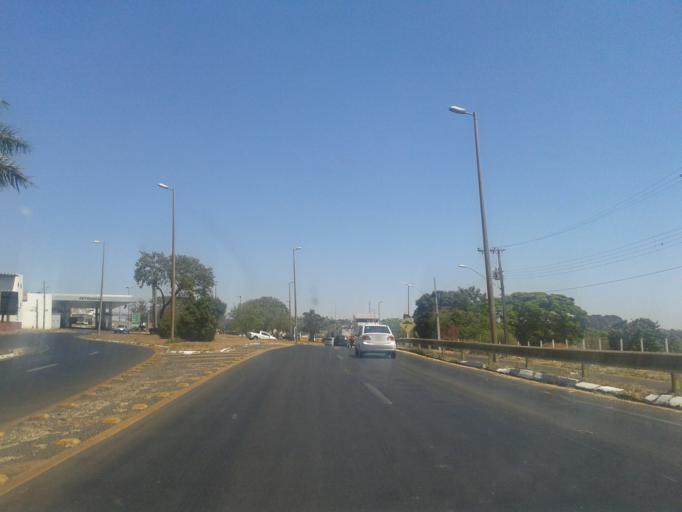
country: BR
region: Minas Gerais
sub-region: Uberlandia
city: Uberlandia
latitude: -18.9091
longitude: -48.3030
